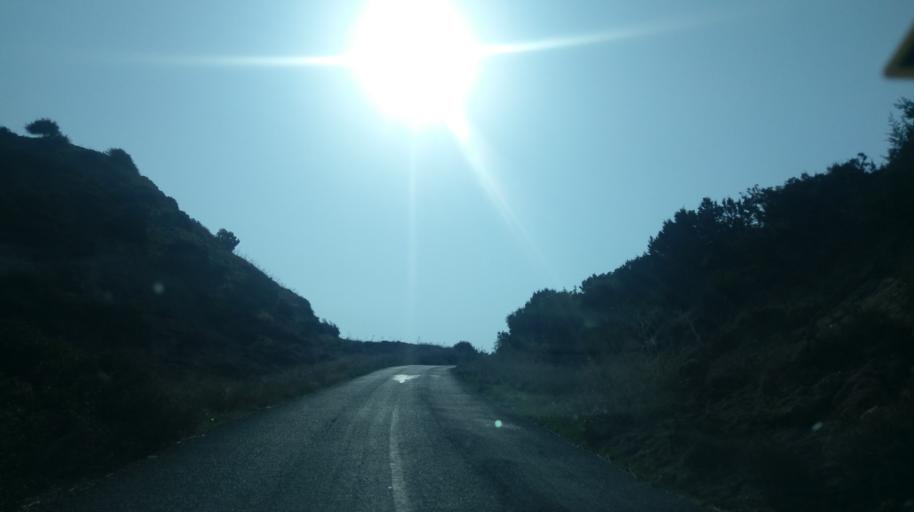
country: CY
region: Ammochostos
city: Rizokarpaso
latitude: 35.5271
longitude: 34.3269
